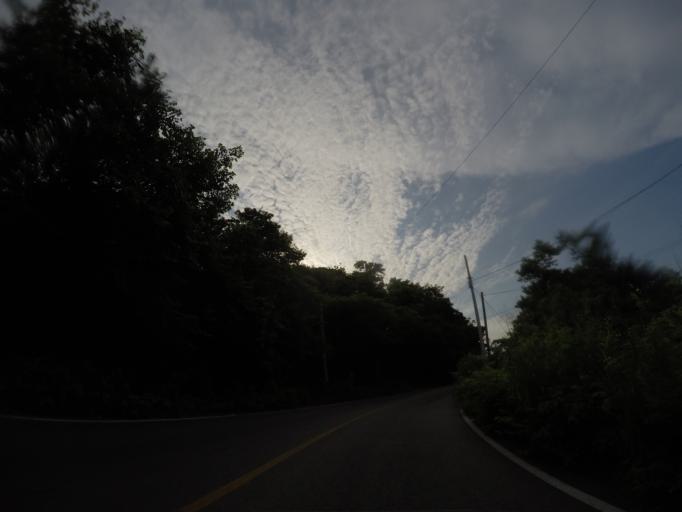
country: MX
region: Oaxaca
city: San Pedro Pochutla
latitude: 15.6999
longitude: -96.4824
